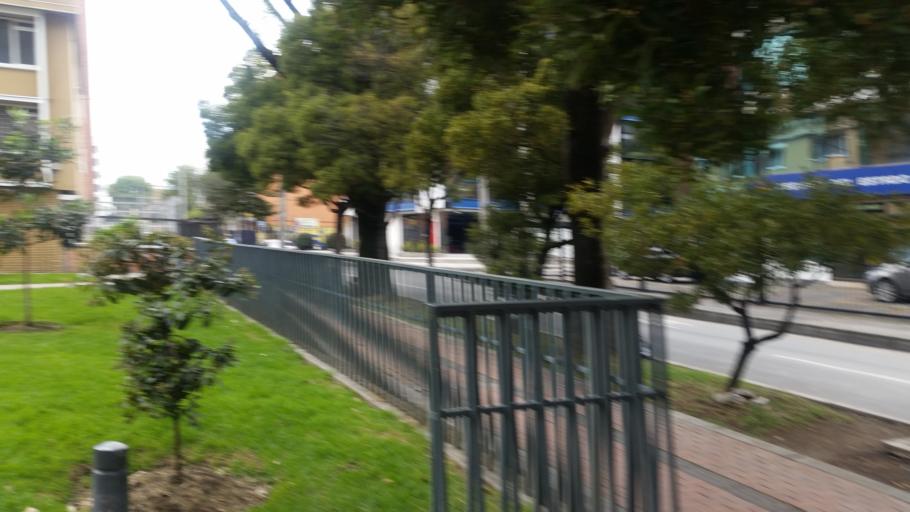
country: CO
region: Bogota D.C.
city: Barrio San Luis
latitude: 4.6699
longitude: -74.0579
